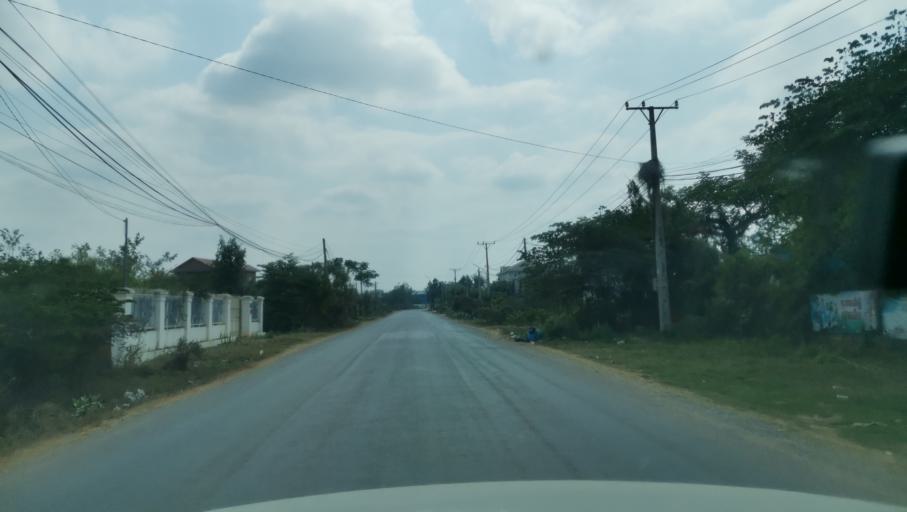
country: KH
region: Battambang
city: Battambang
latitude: 13.0802
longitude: 103.1857
